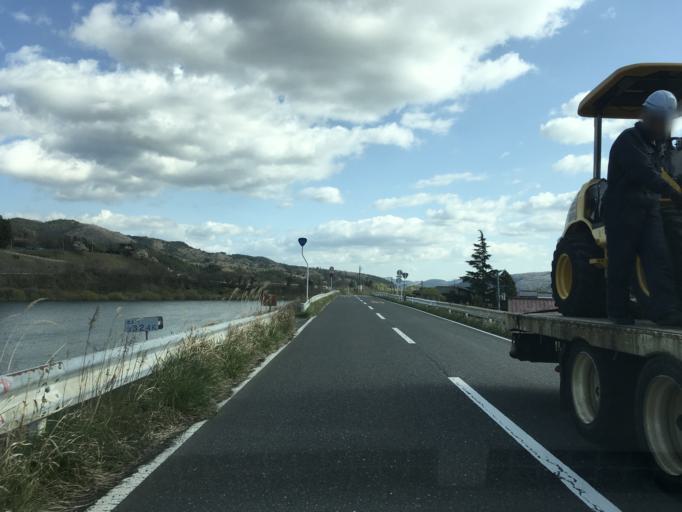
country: JP
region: Miyagi
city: Wakuya
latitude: 38.6611
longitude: 141.2855
